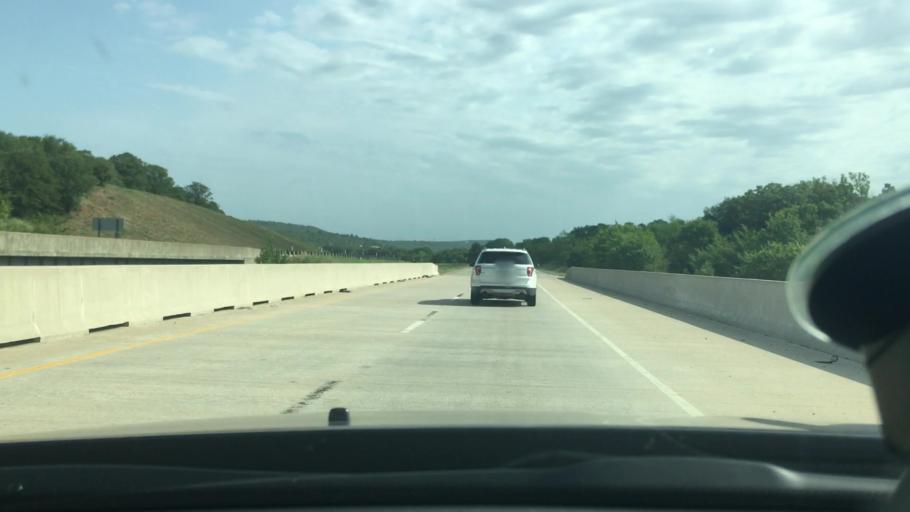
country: US
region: Oklahoma
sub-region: Atoka County
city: Atoka
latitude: 34.4404
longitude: -96.0734
